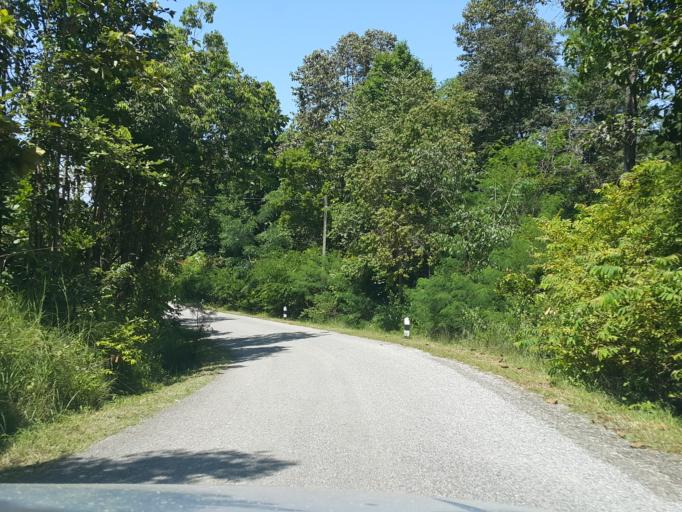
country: TH
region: Chiang Mai
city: San Kamphaeng
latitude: 18.7097
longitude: 99.1816
